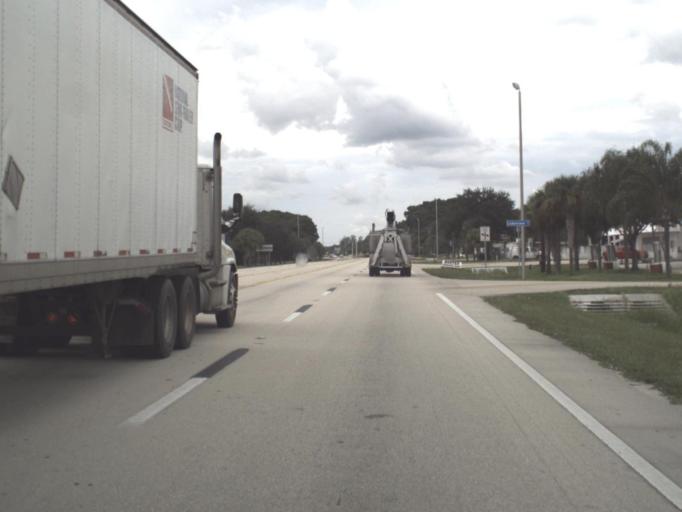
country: US
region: Florida
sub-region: Lee County
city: Fort Myers Shores
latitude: 26.7034
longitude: -81.7530
